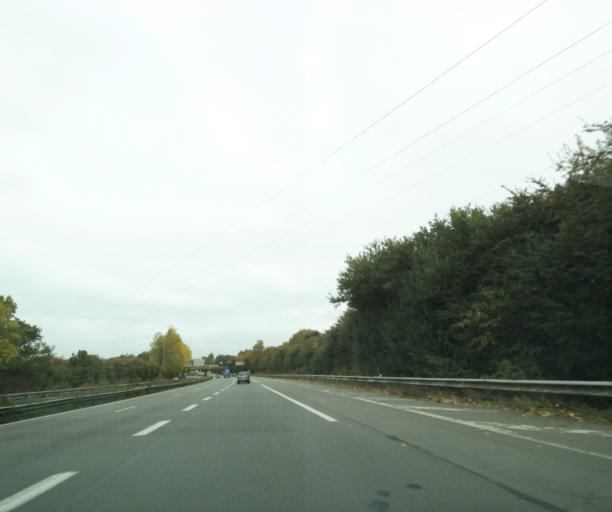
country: FR
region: Nord-Pas-de-Calais
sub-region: Departement du Nord
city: Sainghin-en-Melantois
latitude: 50.5915
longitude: 3.1486
